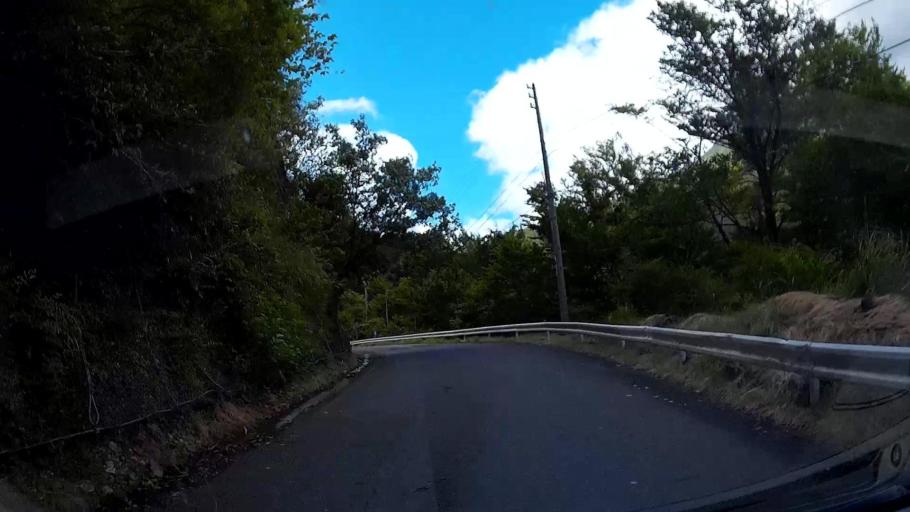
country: JP
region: Shizuoka
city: Shizuoka-shi
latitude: 35.2799
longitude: 138.2192
